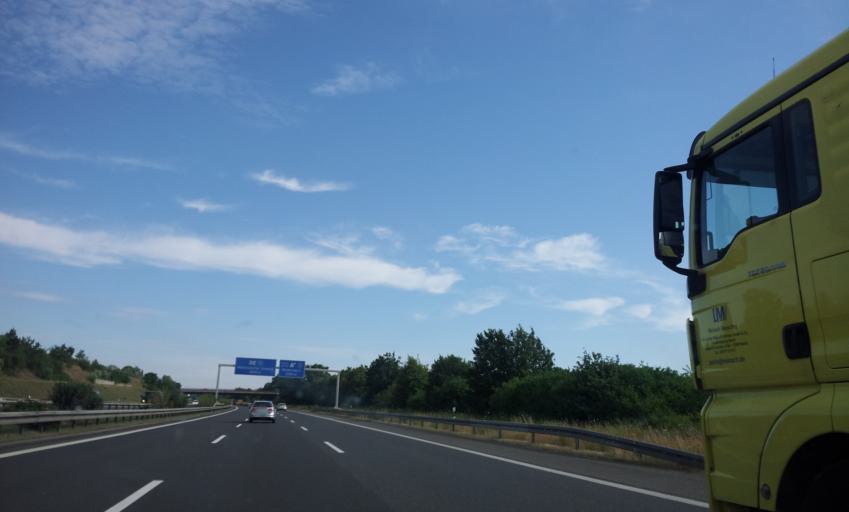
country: DE
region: Brandenburg
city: Schulzendorf
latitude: 52.3396
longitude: 13.5549
